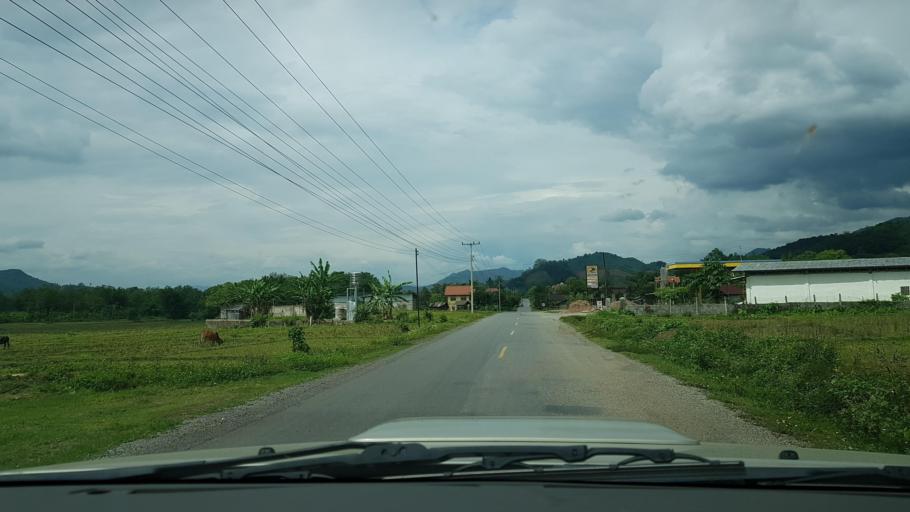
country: LA
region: Loungnamtha
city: Muang Nale
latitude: 20.3254
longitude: 101.6646
